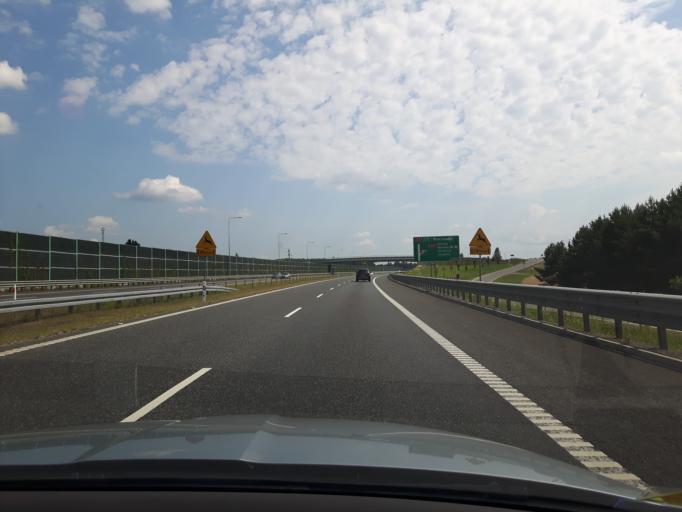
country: PL
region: Warmian-Masurian Voivodeship
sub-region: Powiat olsztynski
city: Olsztynek
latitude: 53.5870
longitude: 20.2412
